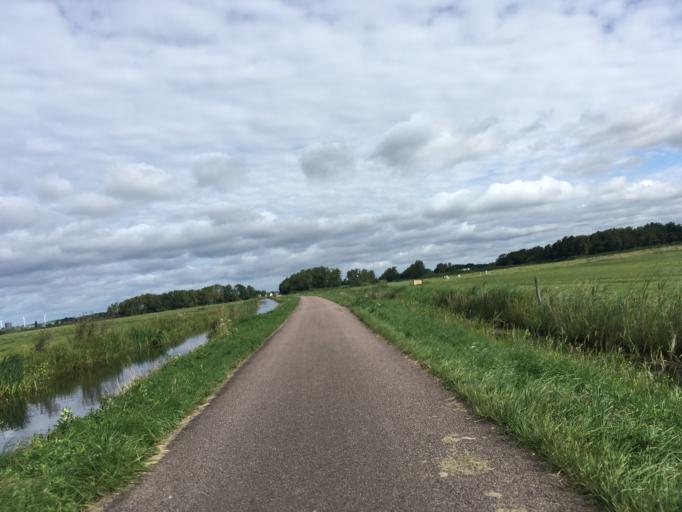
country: NL
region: North Holland
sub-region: Gemeente Haarlem
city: Haarlem
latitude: 52.3883
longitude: 4.7006
